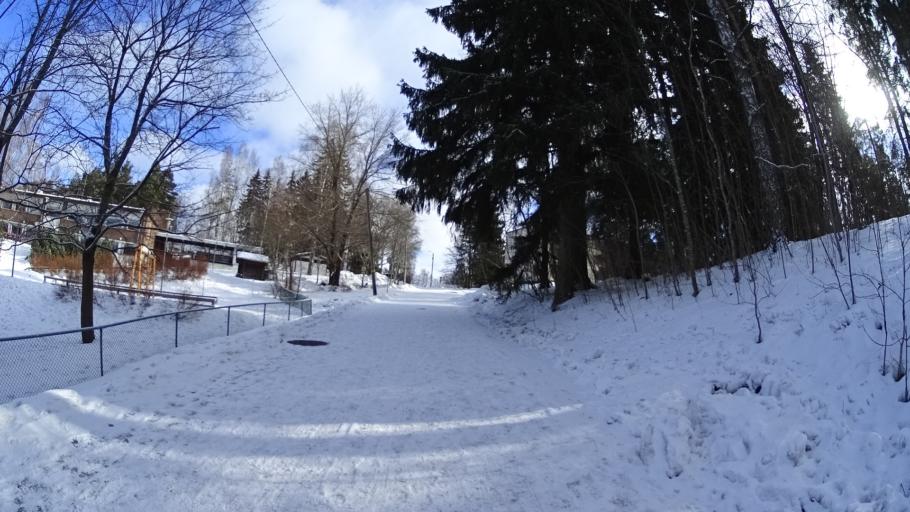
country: FI
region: Uusimaa
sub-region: Helsinki
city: Teekkarikylae
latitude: 60.2659
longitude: 24.8673
